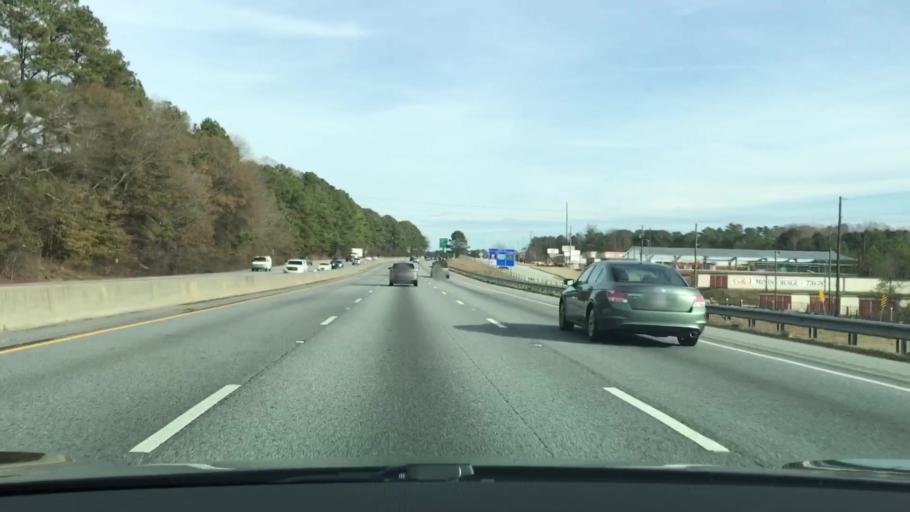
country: US
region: Georgia
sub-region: Newton County
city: Oxford
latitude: 33.6131
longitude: -83.8992
